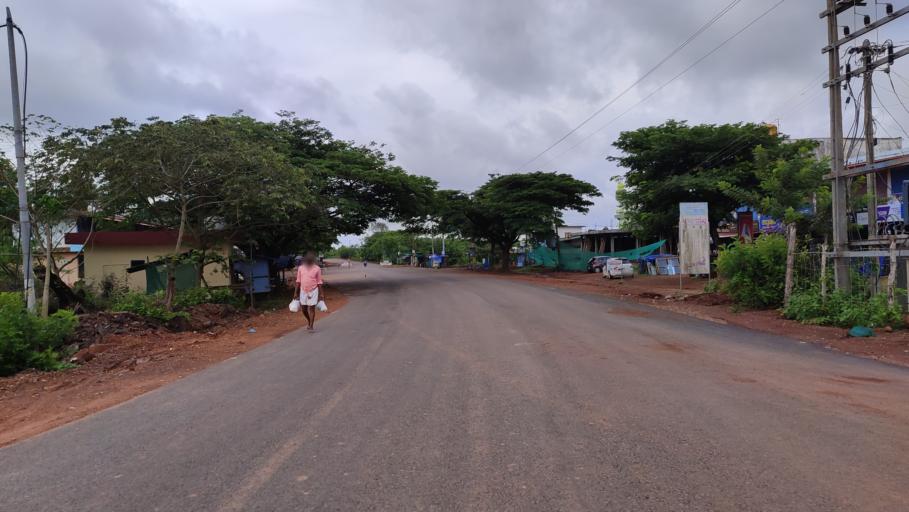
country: IN
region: Kerala
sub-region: Kasaragod District
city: Kasaragod
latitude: 12.5456
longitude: 75.0710
